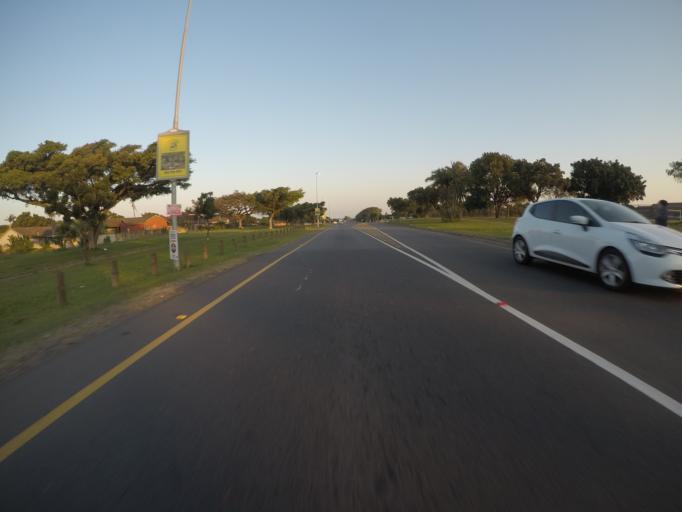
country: ZA
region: KwaZulu-Natal
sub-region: uThungulu District Municipality
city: Richards Bay
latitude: -28.7596
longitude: 32.0588
